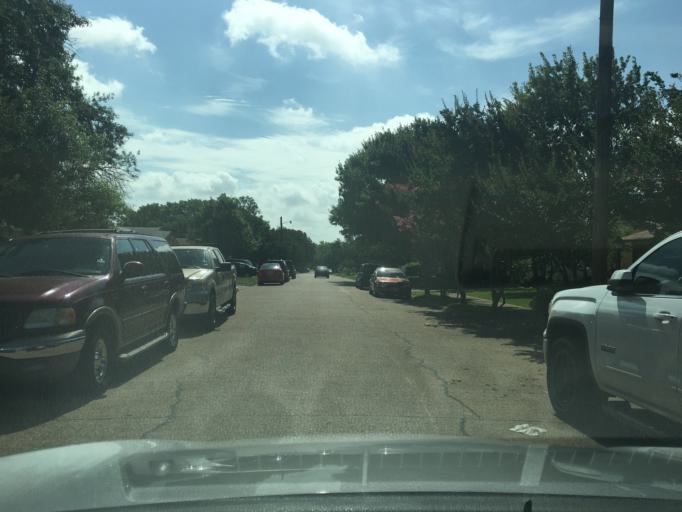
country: US
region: Texas
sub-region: Dallas County
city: Richardson
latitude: 32.9145
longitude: -96.6997
